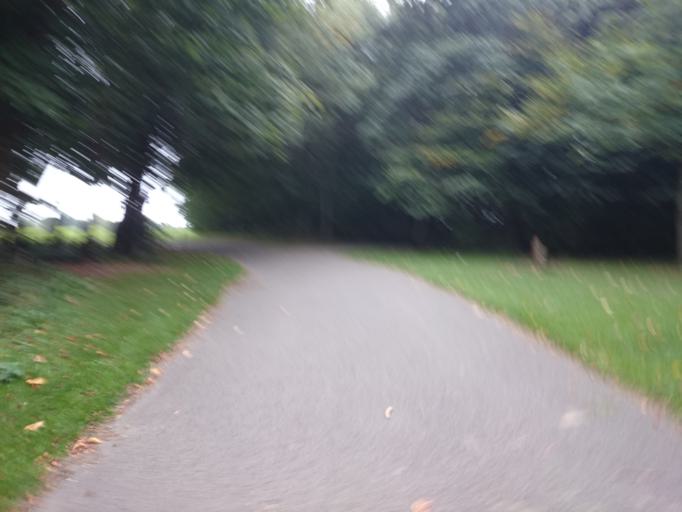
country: IE
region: Leinster
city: Shankill
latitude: 53.2255
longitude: -6.1173
